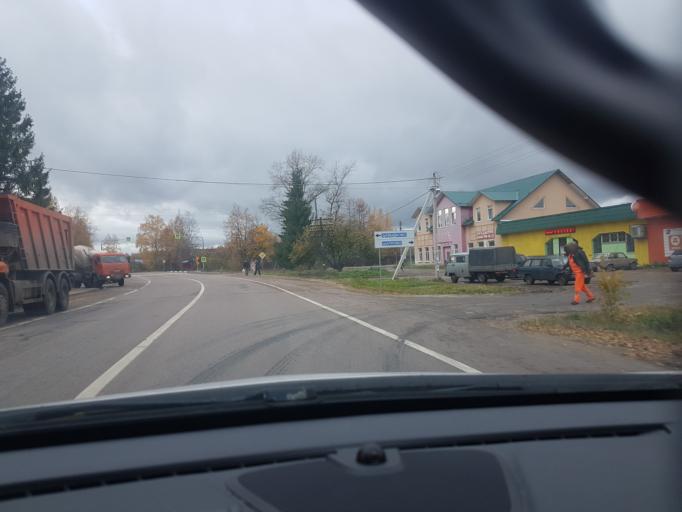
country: RU
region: Moskovskaya
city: Novopetrovskoye
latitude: 56.0085
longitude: 36.3460
